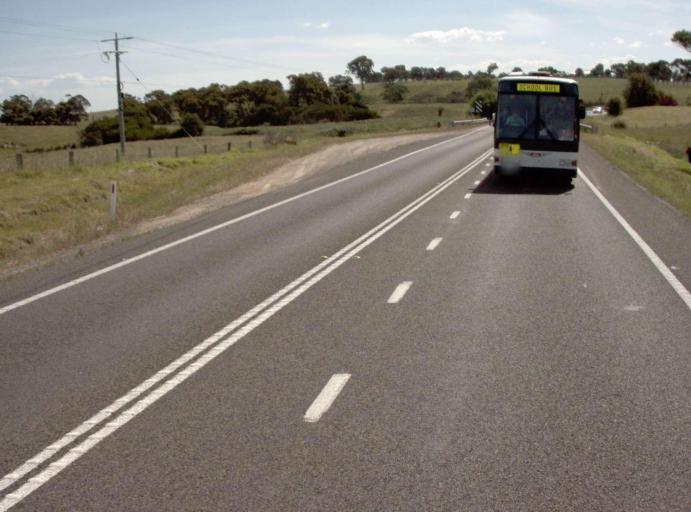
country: AU
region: Victoria
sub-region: East Gippsland
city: Bairnsdale
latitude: -37.8228
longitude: 147.7988
